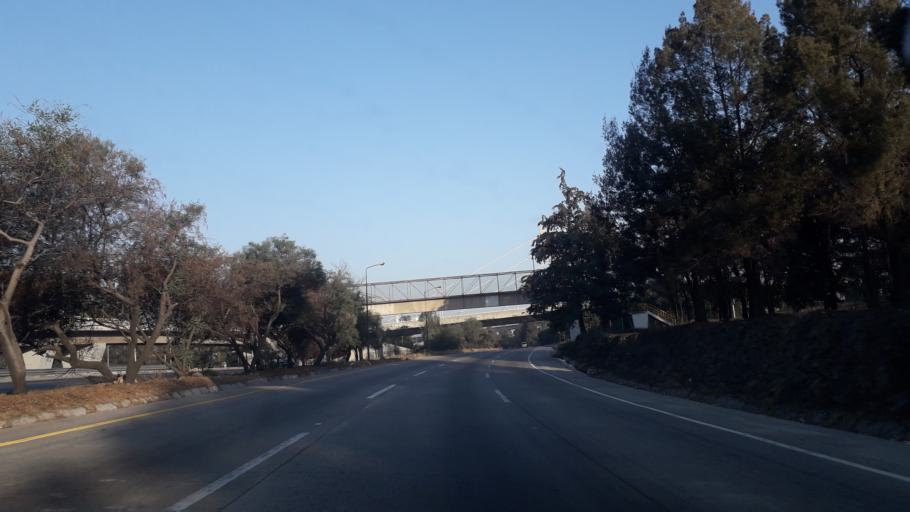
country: MX
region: Puebla
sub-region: Puebla
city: San Sebastian de Aparicio
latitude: 19.0800
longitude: -98.1635
